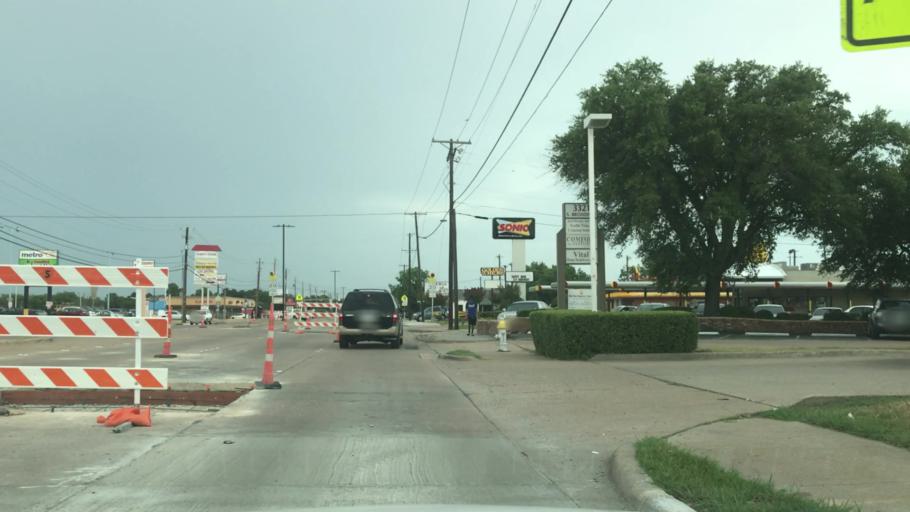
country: US
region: Texas
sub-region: Dallas County
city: Garland
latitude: 32.8757
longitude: -96.6180
